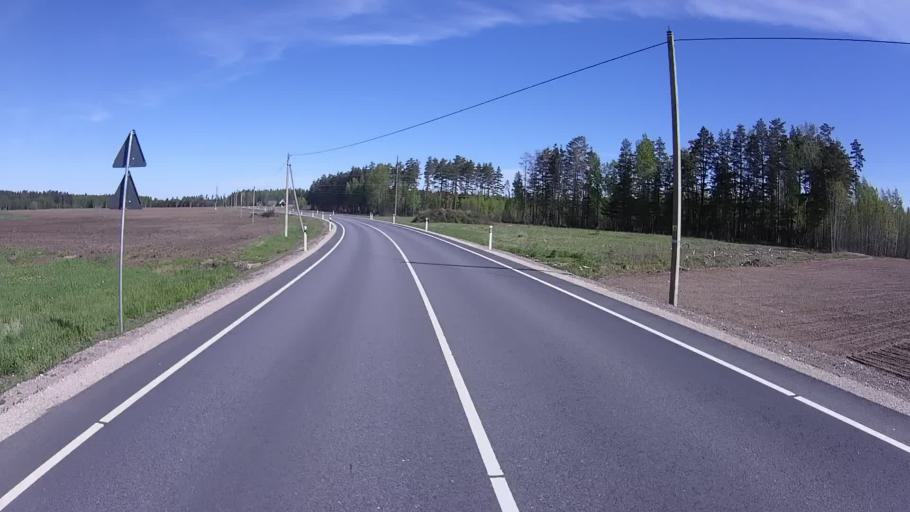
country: RU
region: Pskov
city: Pechory
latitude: 57.9493
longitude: 27.5855
